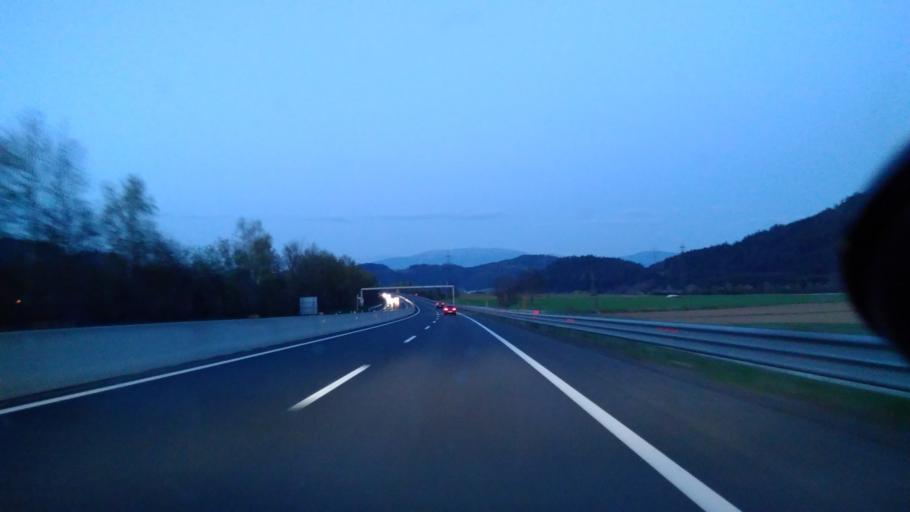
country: AT
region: Carinthia
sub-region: Politischer Bezirk Volkermarkt
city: Griffen
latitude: 46.6882
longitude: 14.7008
